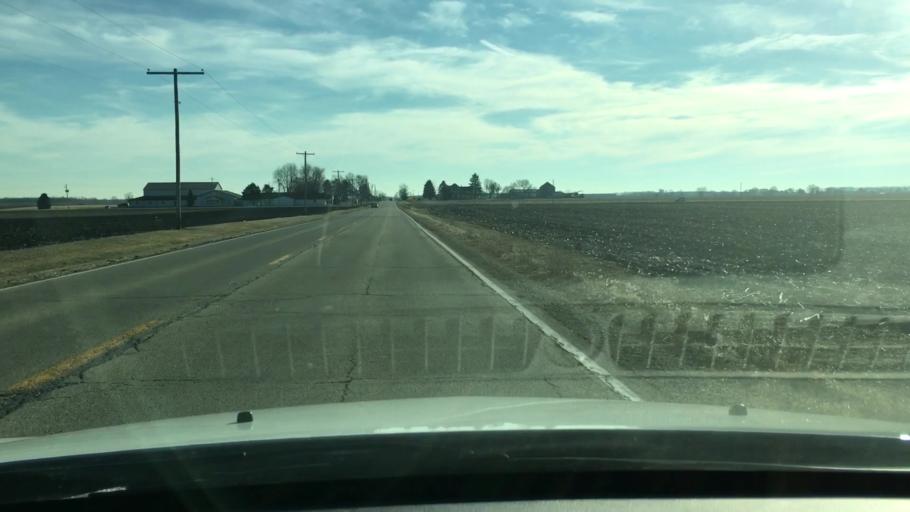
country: US
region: Illinois
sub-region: LaSalle County
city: Peru
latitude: 41.3996
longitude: -89.1260
